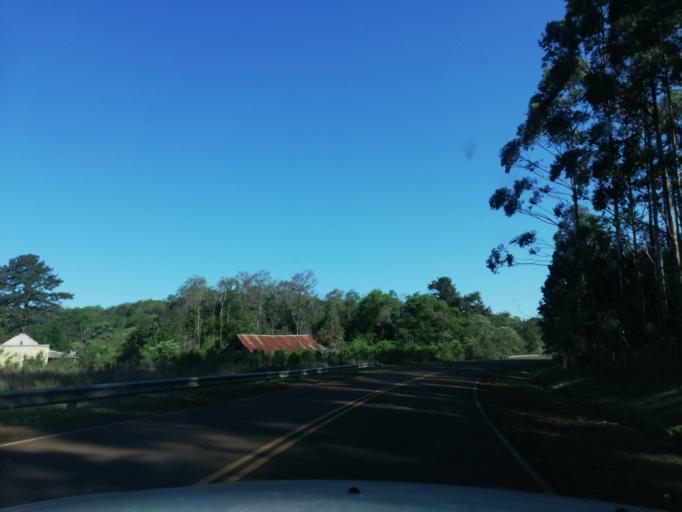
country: AR
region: Misiones
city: Arroyo del Medio
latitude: -27.6509
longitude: -55.4007
